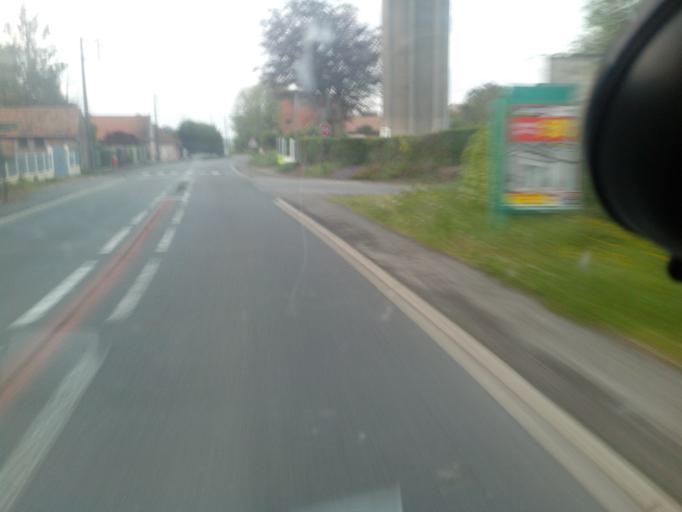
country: FR
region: Nord-Pas-de-Calais
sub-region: Departement du Pas-de-Calais
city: Marconnelle
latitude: 50.3106
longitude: 2.0106
